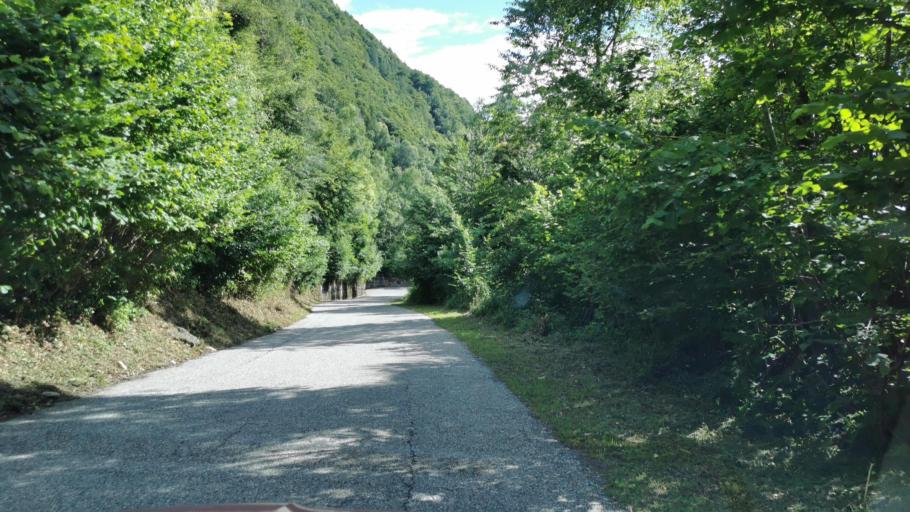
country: IT
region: Lombardy
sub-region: Provincia di Lecco
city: Casargo
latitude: 46.0387
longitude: 9.3960
